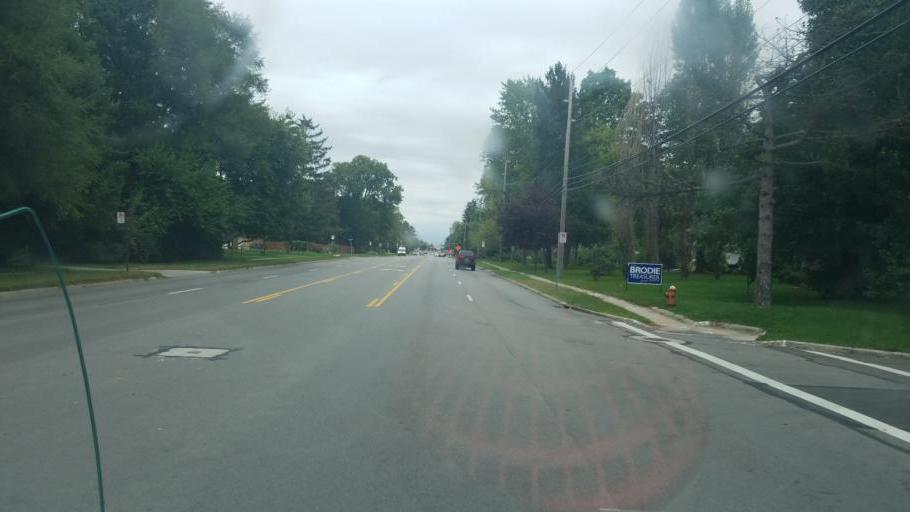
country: US
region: Ohio
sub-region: Lucas County
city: Ottawa Hills
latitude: 41.6771
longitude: -83.6355
